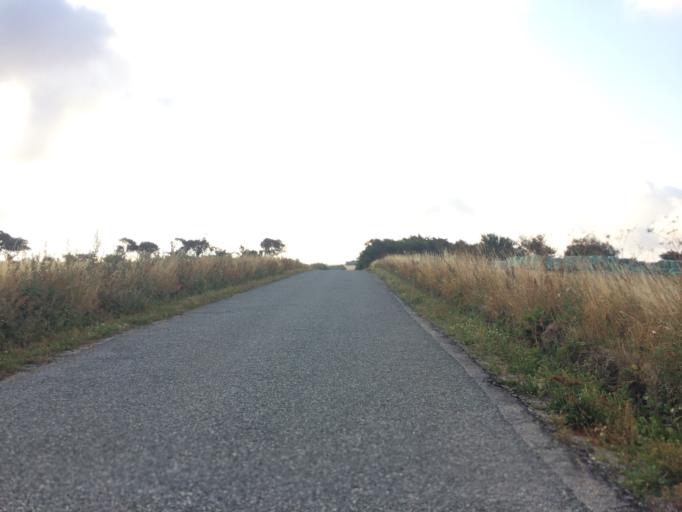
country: DK
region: Central Jutland
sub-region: Holstebro Kommune
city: Vinderup
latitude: 56.6053
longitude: 8.7048
